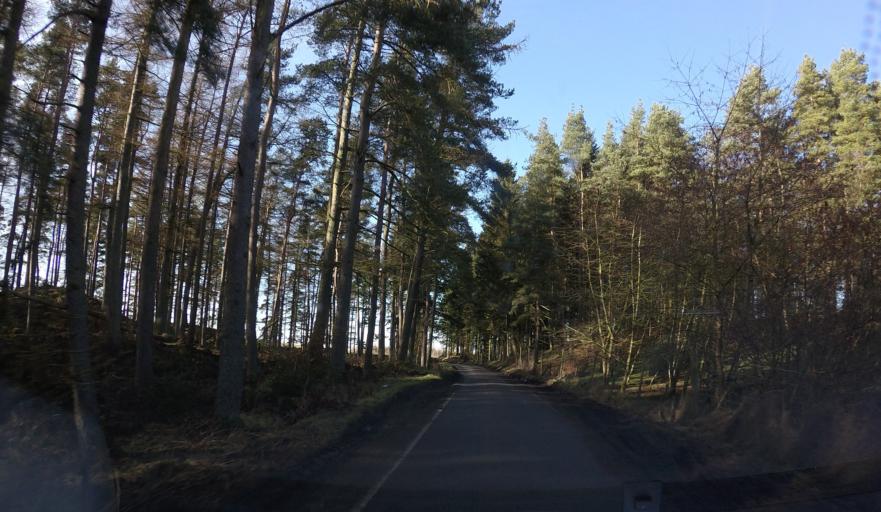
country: GB
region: Scotland
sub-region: Perth and Kinross
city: Stanley
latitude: 56.5270
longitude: -3.4208
